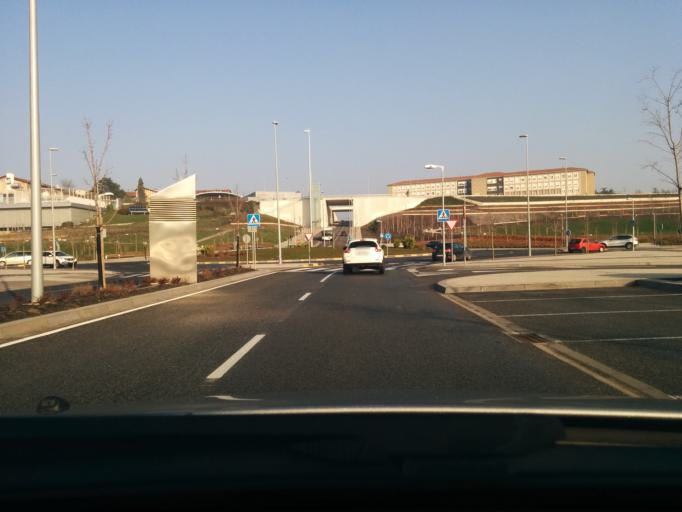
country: ES
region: Navarre
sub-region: Provincia de Navarra
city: Segundo Ensanche
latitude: 42.8097
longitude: -1.6267
